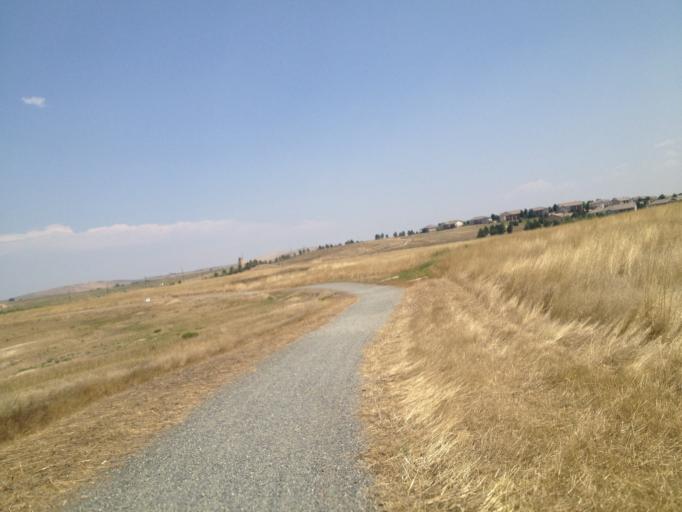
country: US
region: Colorado
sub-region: Boulder County
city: Lafayette
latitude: 39.9969
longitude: -105.0567
